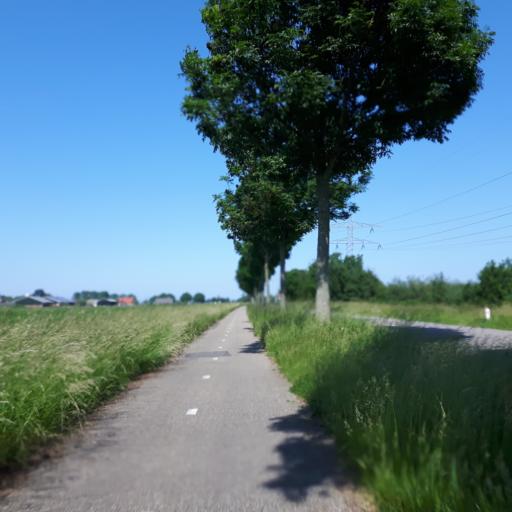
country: NL
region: Utrecht
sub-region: Gemeente Utrecht
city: Utrecht
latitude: 52.1340
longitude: 5.1077
